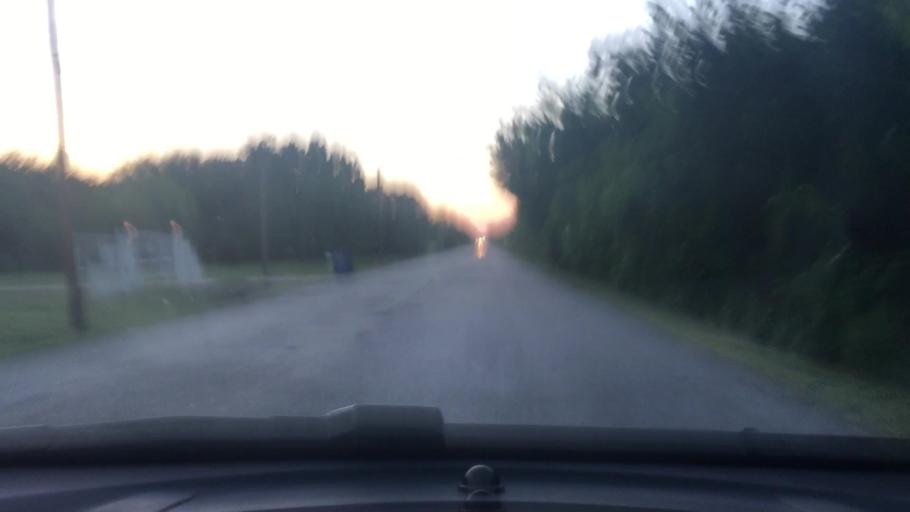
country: US
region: Texas
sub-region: Ellis County
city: Red Oak
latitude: 32.5607
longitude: -96.8090
